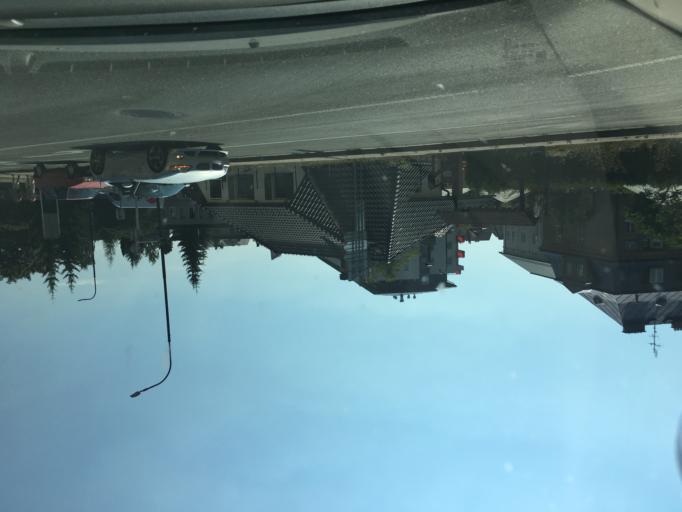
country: CZ
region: Kralovehradecky
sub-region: Okres Trutnov
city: Vrchlabi
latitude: 50.6193
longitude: 15.6087
